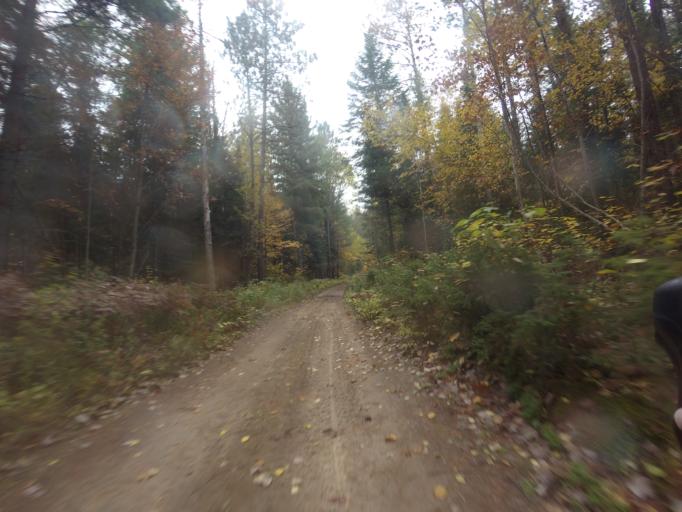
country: CA
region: Ontario
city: Petawawa
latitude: 45.7741
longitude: -77.3754
